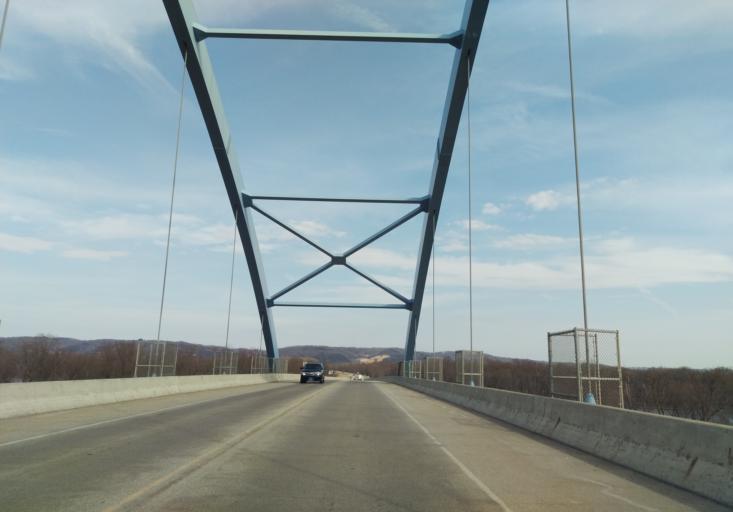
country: US
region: Wisconsin
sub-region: Crawford County
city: Prairie du Chien
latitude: 43.0440
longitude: -91.1762
